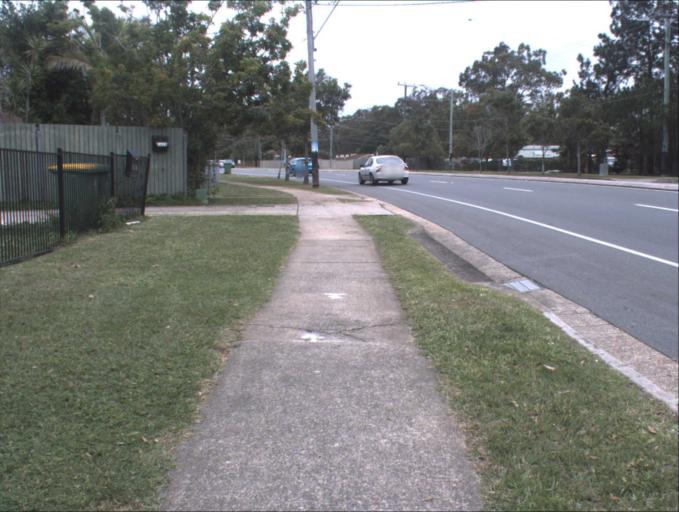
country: AU
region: Queensland
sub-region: Logan
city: Park Ridge South
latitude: -27.6807
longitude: 153.0194
